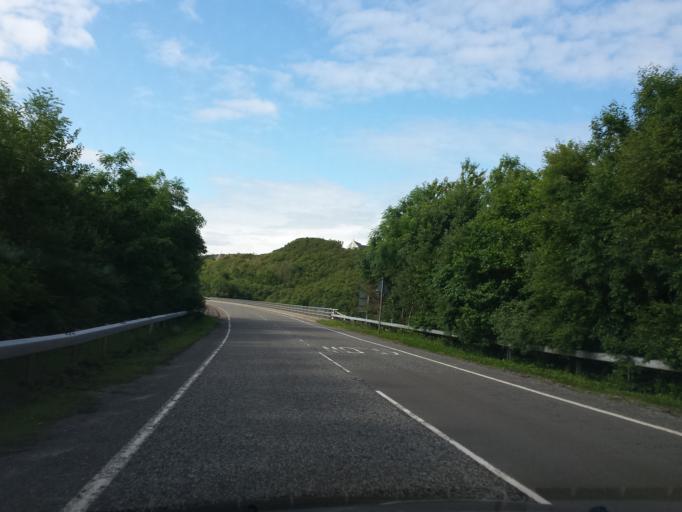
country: GB
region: Scotland
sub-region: Argyll and Bute
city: Isle Of Mull
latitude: 56.9610
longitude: -5.8189
